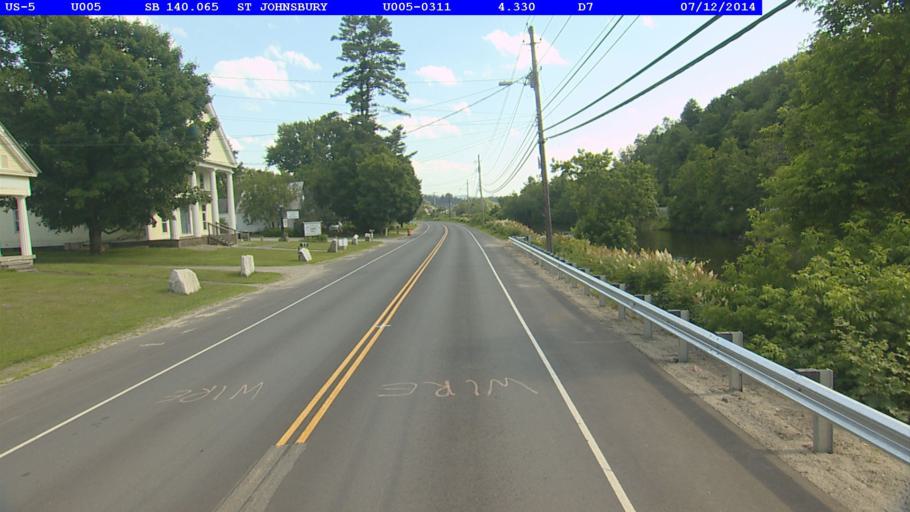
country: US
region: Vermont
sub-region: Caledonia County
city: St Johnsbury
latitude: 44.4536
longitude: -72.0165
